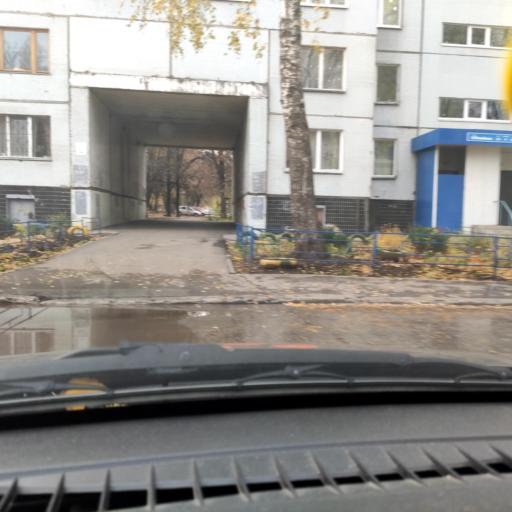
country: RU
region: Samara
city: Tol'yatti
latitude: 53.5250
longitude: 49.2833
